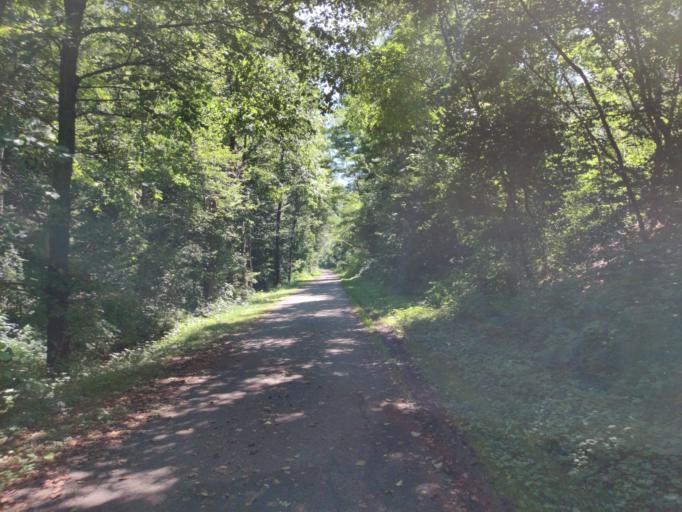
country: AT
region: Styria
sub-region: Politischer Bezirk Leibnitz
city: Ehrenhausen
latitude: 46.7275
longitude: 15.5929
